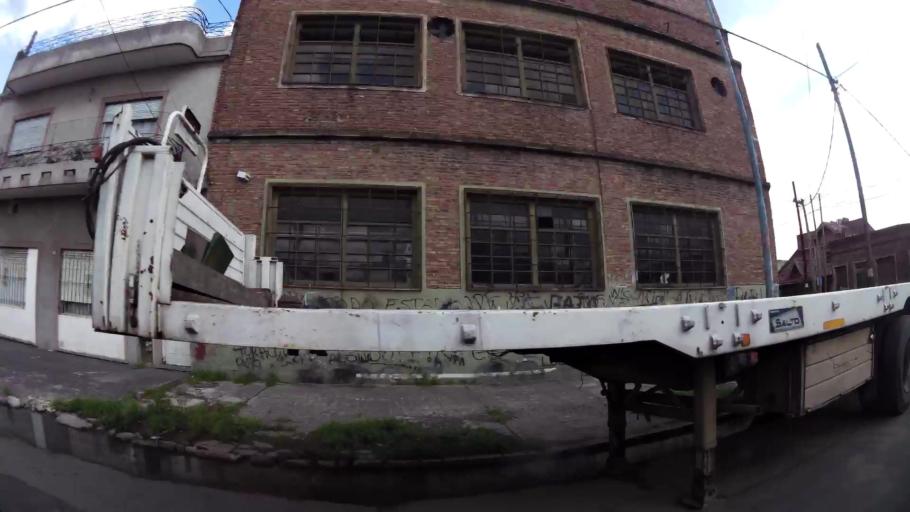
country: AR
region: Buenos Aires
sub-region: Partido de Lanus
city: Lanus
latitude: -34.6780
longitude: -58.4103
